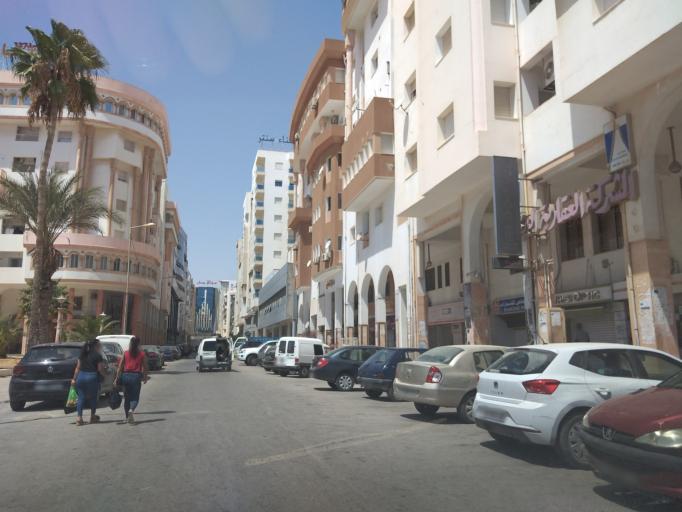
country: TN
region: Safaqis
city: Sfax
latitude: 34.7399
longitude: 10.7576
